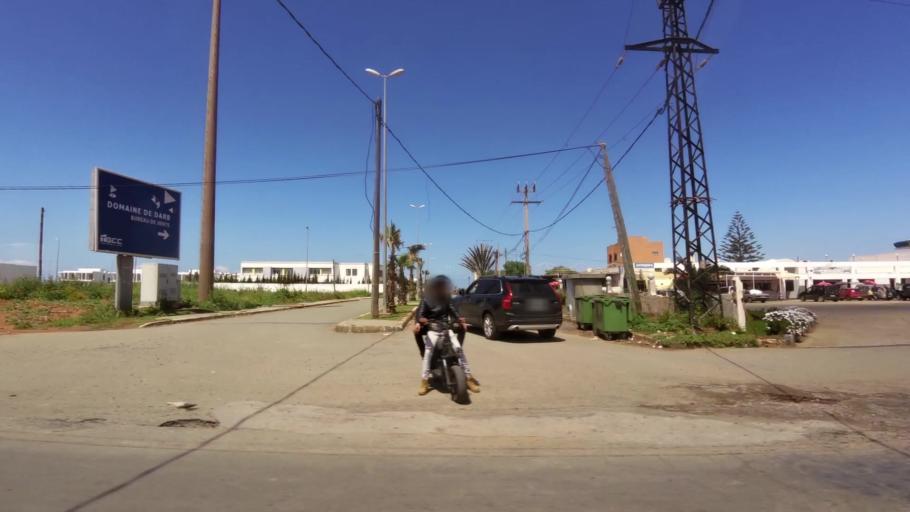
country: MA
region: Grand Casablanca
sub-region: Nouaceur
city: Dar Bouazza
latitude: 33.5235
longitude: -7.7859
